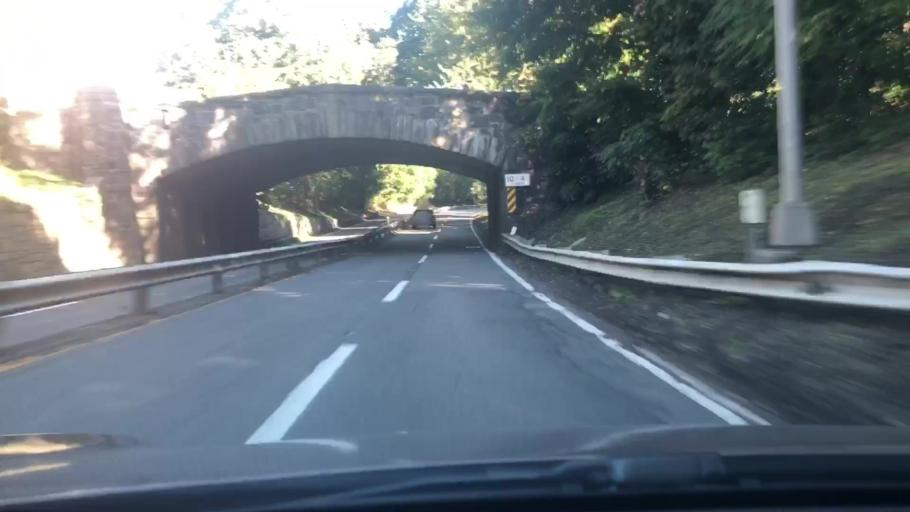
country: US
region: New York
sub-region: Westchester County
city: Bronxville
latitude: 40.9410
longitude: -73.8390
